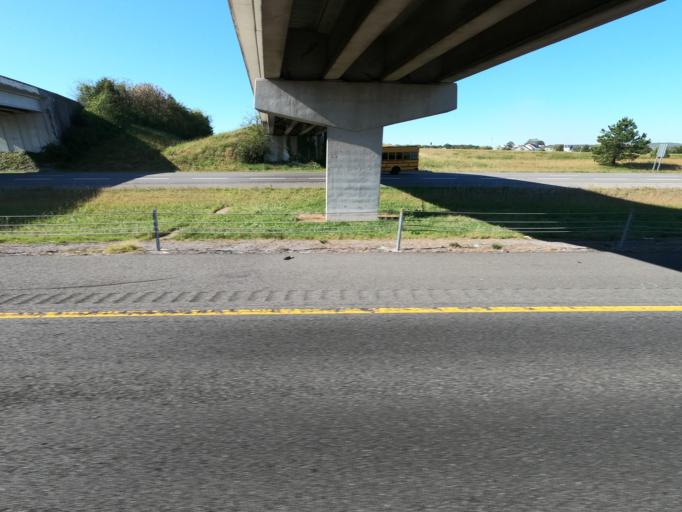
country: US
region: Tennessee
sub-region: Rutherford County
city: Murfreesboro
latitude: 35.8857
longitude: -86.4771
